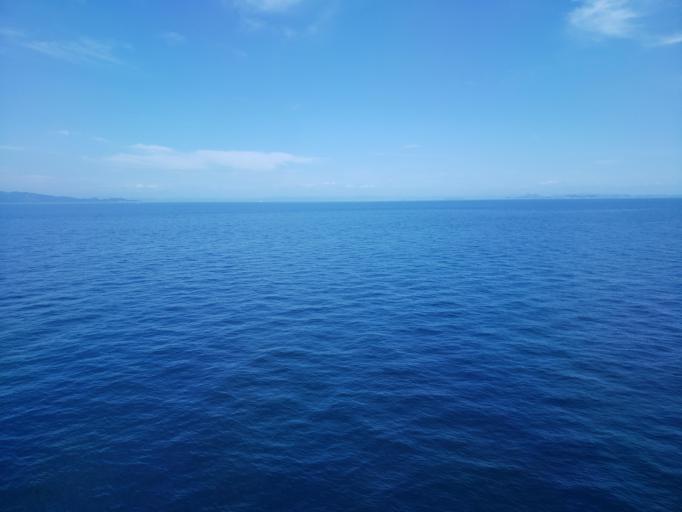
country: JP
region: Tokushima
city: Narutocho-mitsuishi
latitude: 34.4617
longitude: 134.4687
